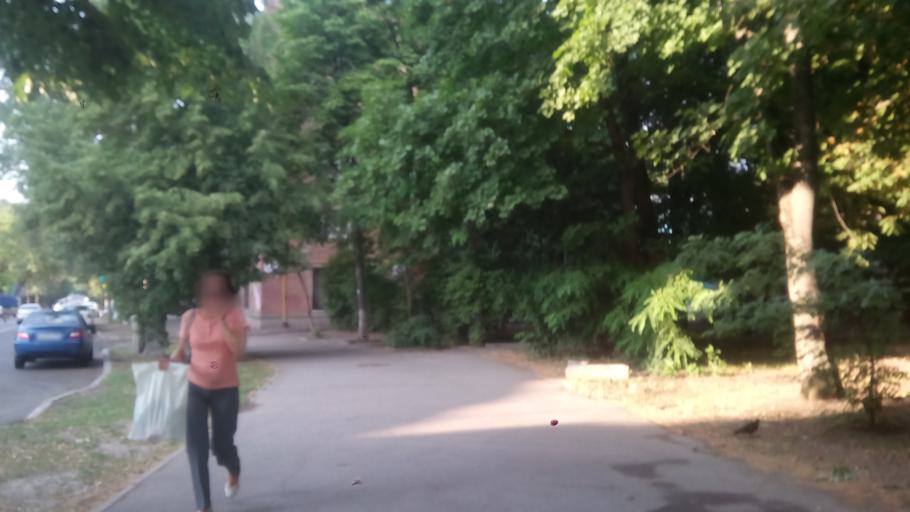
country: RU
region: Rostov
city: Imeni Chkalova
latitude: 47.2536
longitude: 39.7672
